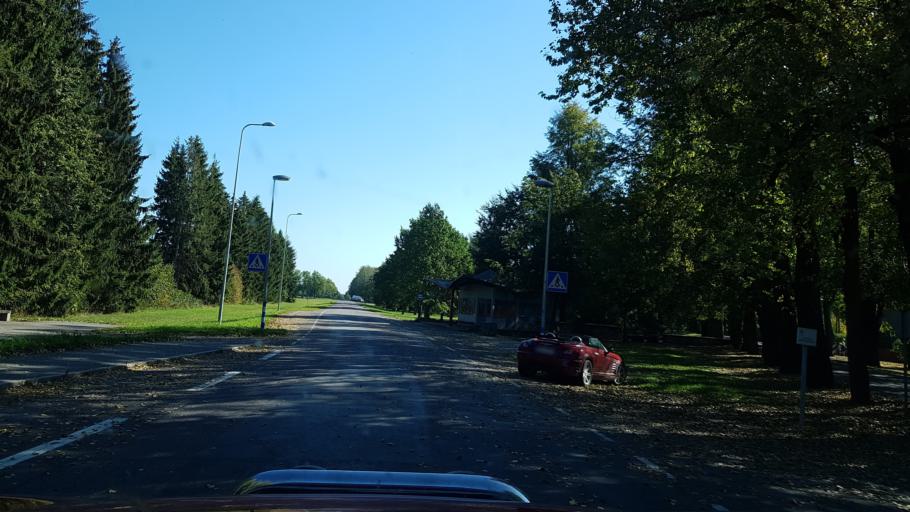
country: EE
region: Tartu
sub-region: Tartu linn
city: Tartu
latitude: 58.3564
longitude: 26.8726
